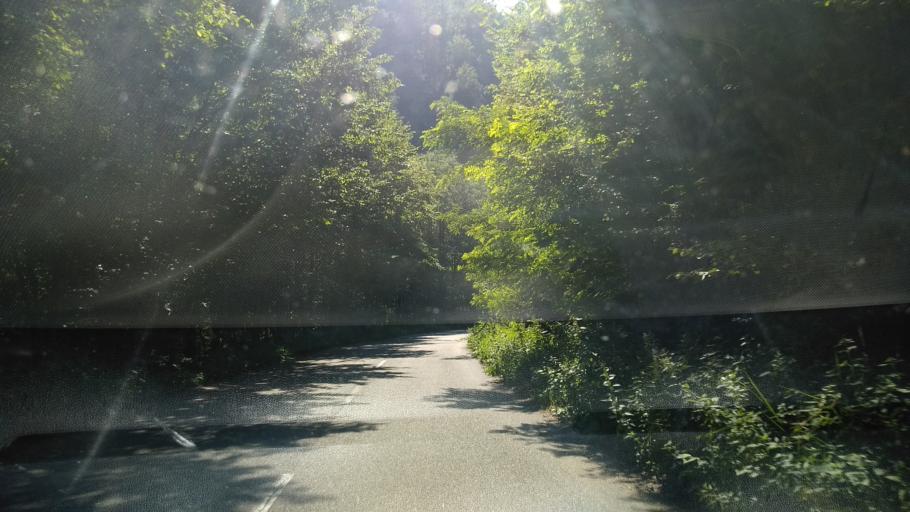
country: RO
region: Hunedoara
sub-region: Comuna Orastioara de Sus
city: Orastioara de Sus
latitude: 45.6510
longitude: 23.1896
